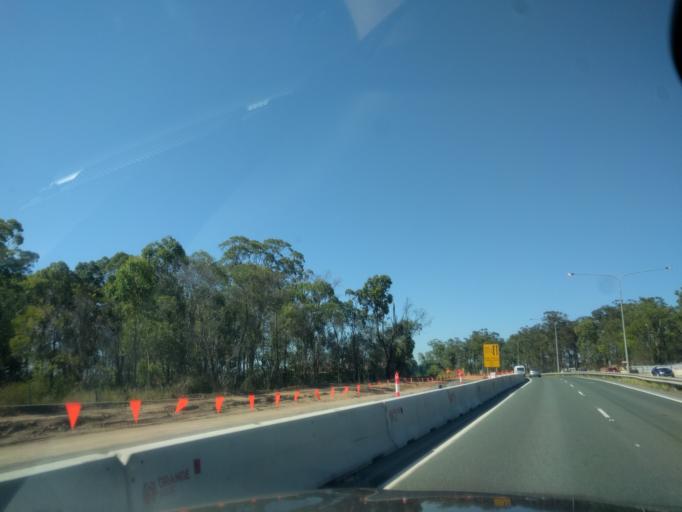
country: AU
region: Queensland
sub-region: Brisbane
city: Sunnybank Hills
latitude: -27.6419
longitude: 153.0435
